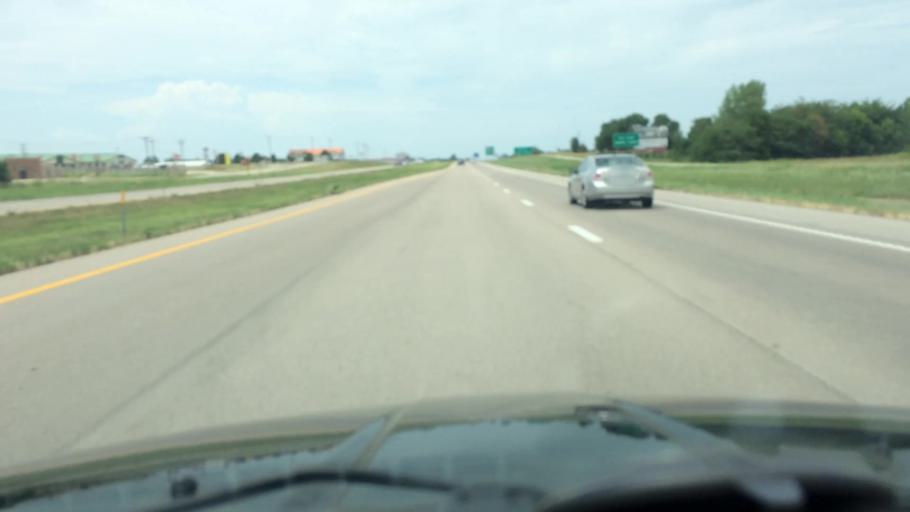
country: US
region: Missouri
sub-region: Polk County
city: Bolivar
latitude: 37.5546
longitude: -93.3880
